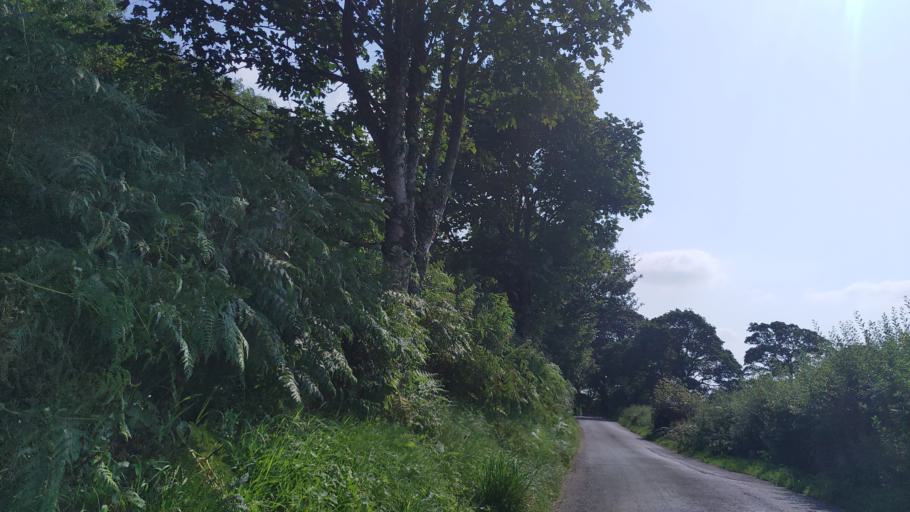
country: GB
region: England
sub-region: Lancashire
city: Clayton-le-Woods
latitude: 53.7009
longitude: -2.6206
